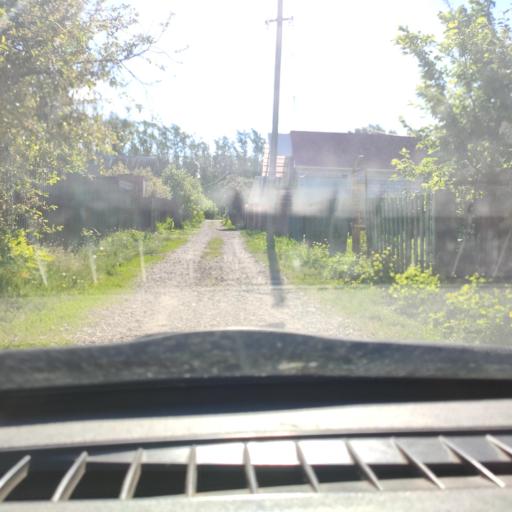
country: RU
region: Samara
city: Tol'yatti
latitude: 53.6264
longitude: 49.4136
